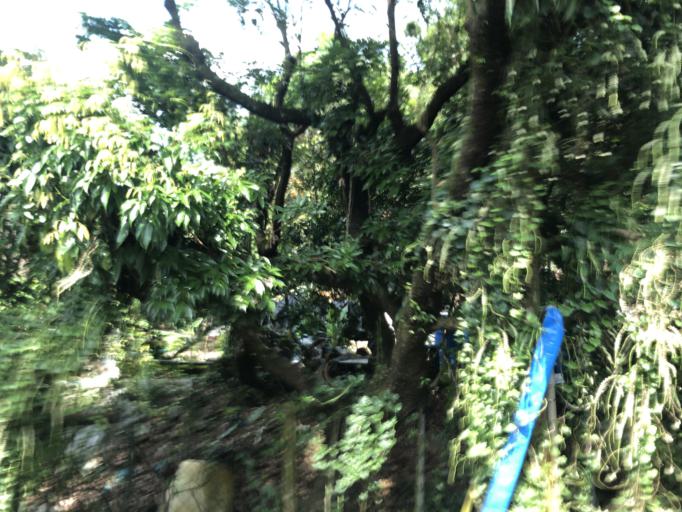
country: TW
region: Taiwan
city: Yujing
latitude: 22.9332
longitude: 120.5886
